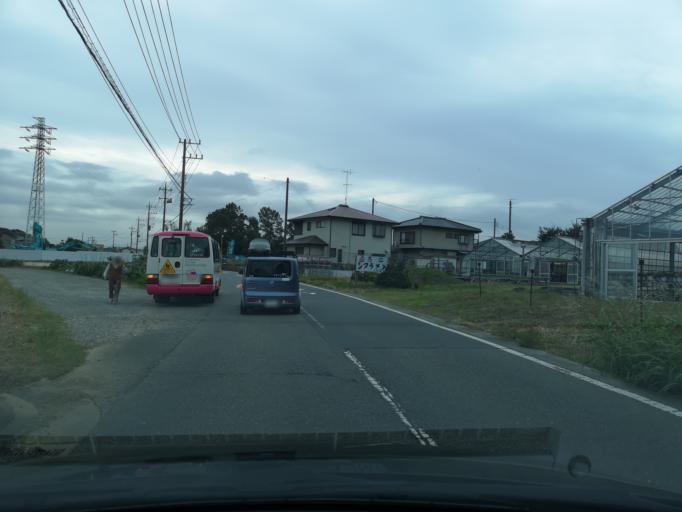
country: JP
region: Kanagawa
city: Atsugi
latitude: 35.3872
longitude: 139.3928
